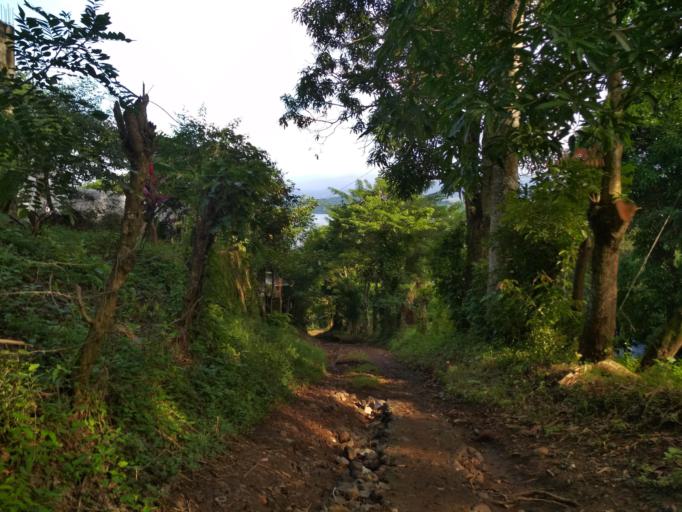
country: MX
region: Veracruz
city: Catemaco
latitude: 18.3914
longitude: -95.1248
